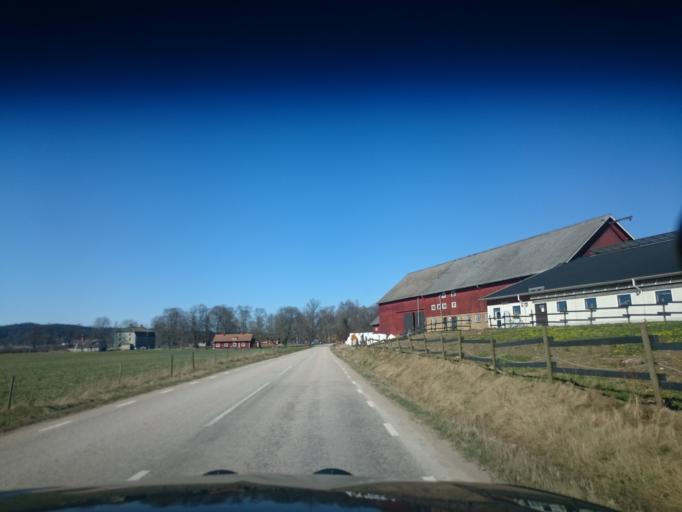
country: SE
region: Kronoberg
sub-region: Vaxjo Kommun
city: Braas
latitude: 57.1942
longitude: 14.9585
